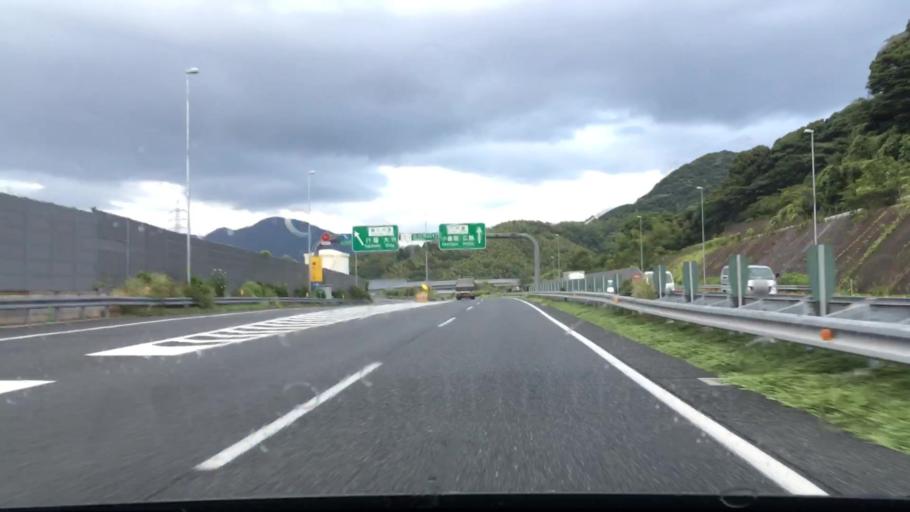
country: JP
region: Fukuoka
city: Kitakyushu
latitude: 33.8123
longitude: 130.8816
